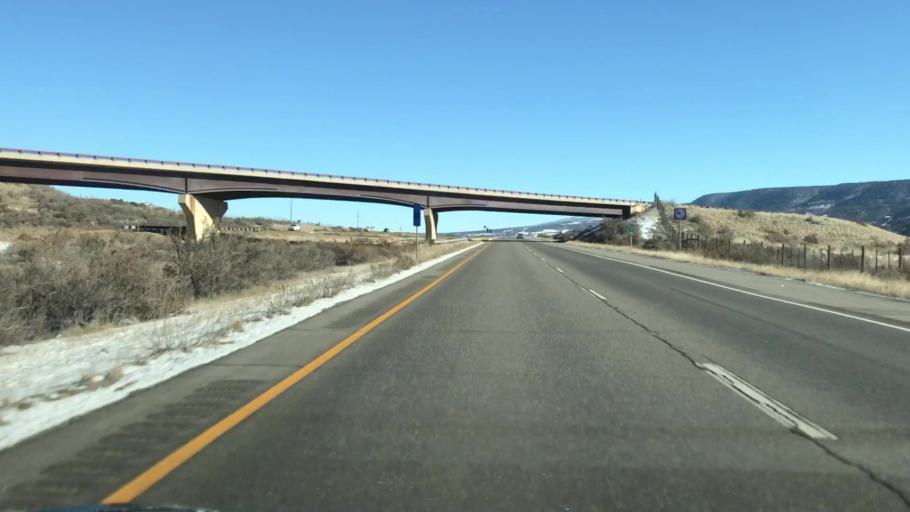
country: US
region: Colorado
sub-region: Garfield County
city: Battlement Mesa
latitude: 39.4765
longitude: -107.9941
